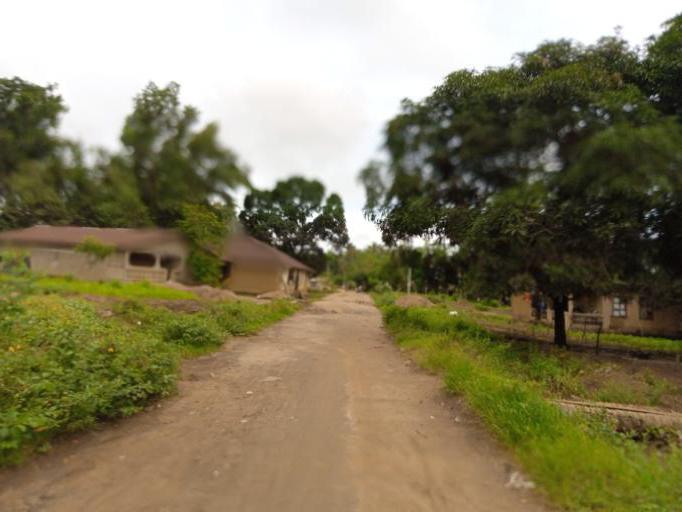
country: SL
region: Northern Province
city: Masoyila
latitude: 8.5958
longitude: -13.1964
